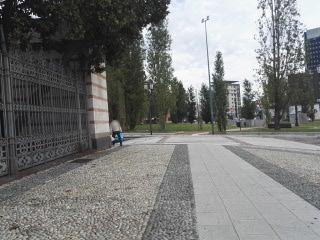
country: IT
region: Lombardy
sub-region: Citta metropolitana di Milano
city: Milano
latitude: 45.4854
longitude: 9.1801
